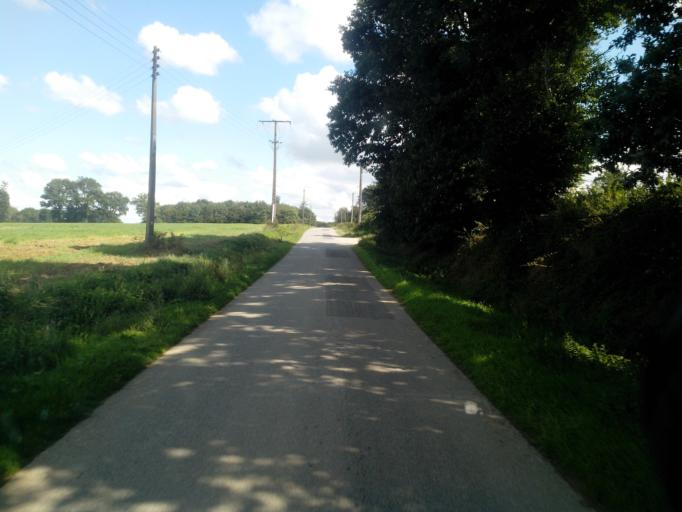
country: FR
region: Brittany
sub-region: Departement du Morbihan
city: Mauron
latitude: 48.1420
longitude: -2.2952
